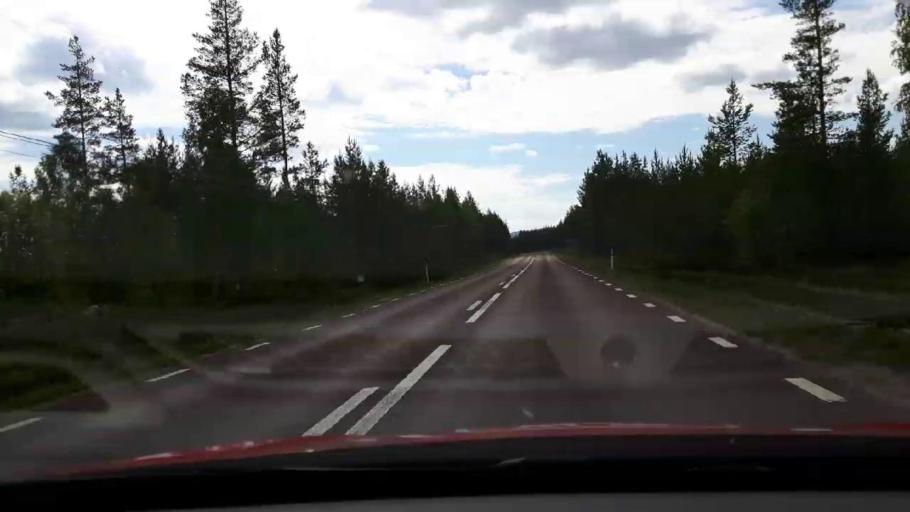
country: SE
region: Jaemtland
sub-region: Harjedalens Kommun
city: Sveg
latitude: 62.1226
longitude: 14.9707
